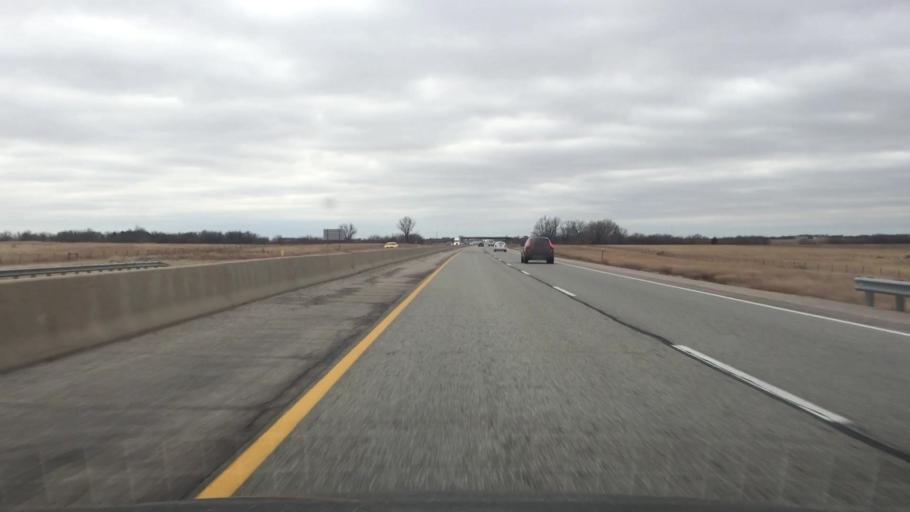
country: US
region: Kansas
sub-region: Butler County
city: El Dorado
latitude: 38.0348
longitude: -96.6534
